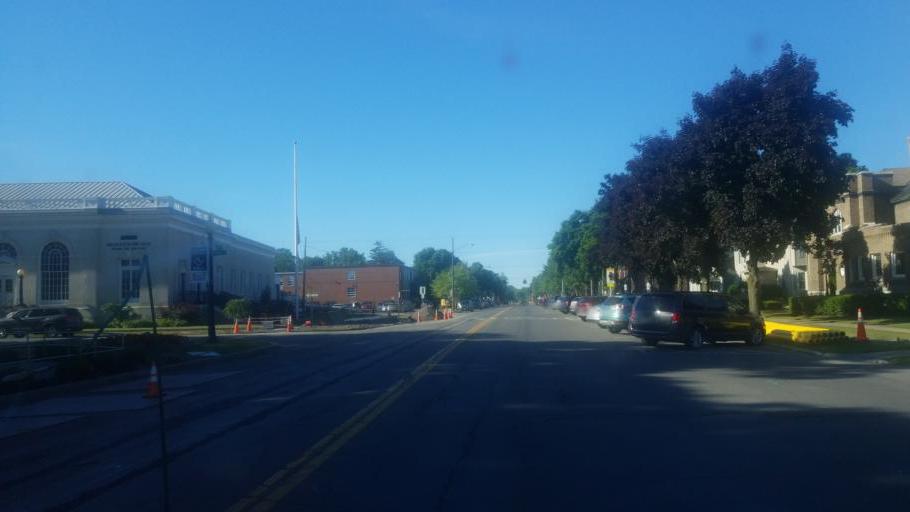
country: US
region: New York
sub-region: Wayne County
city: Newark
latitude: 43.0445
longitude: -77.0953
